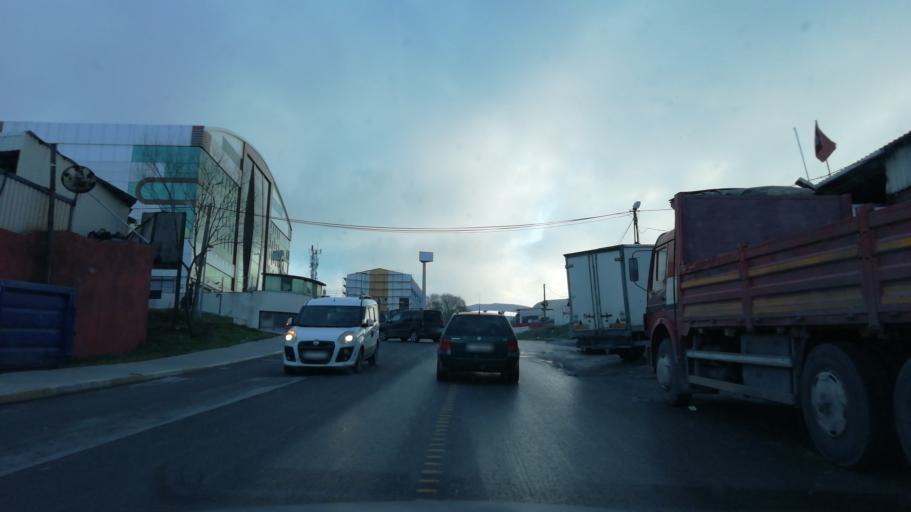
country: TR
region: Istanbul
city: Esenyurt
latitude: 41.0176
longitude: 28.7008
